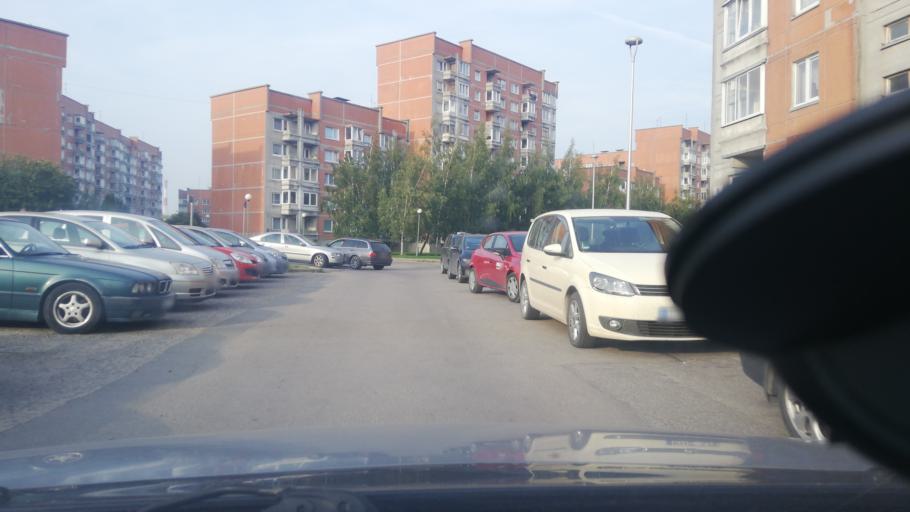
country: LT
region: Klaipedos apskritis
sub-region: Klaipeda
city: Klaipeda
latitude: 55.6669
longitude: 21.1978
